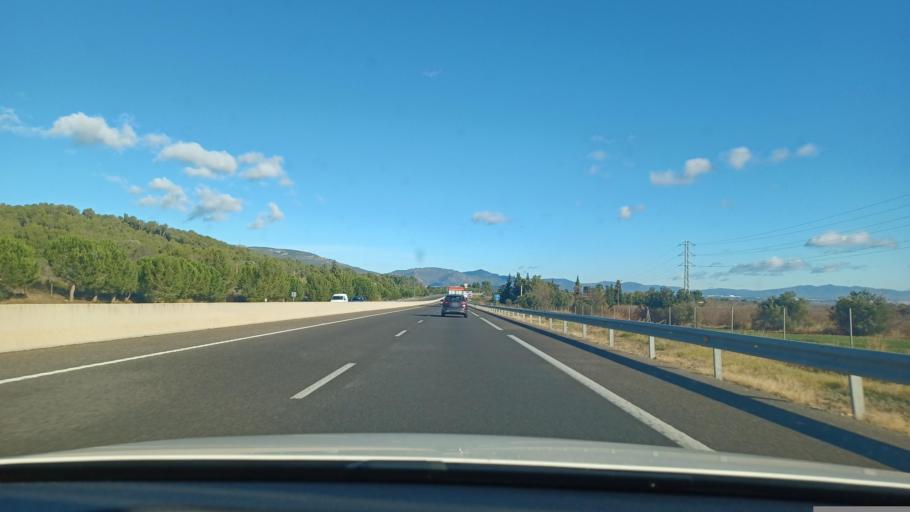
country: ES
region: Catalonia
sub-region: Provincia de Tarragona
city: Alcover
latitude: 41.2374
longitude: 1.1658
